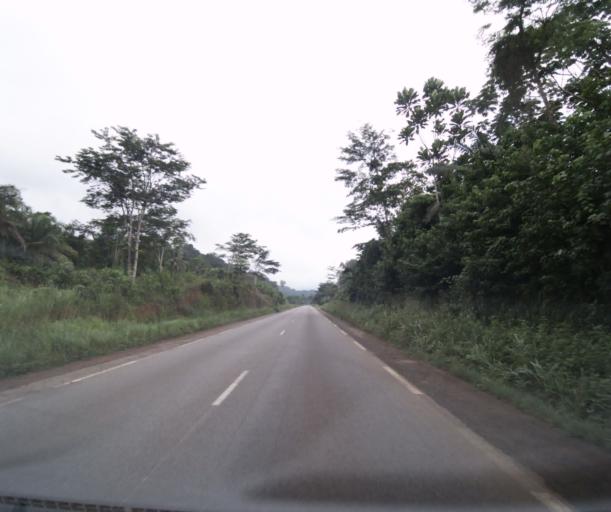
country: CM
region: Littoral
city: Edea
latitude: 3.8033
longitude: 10.2377
